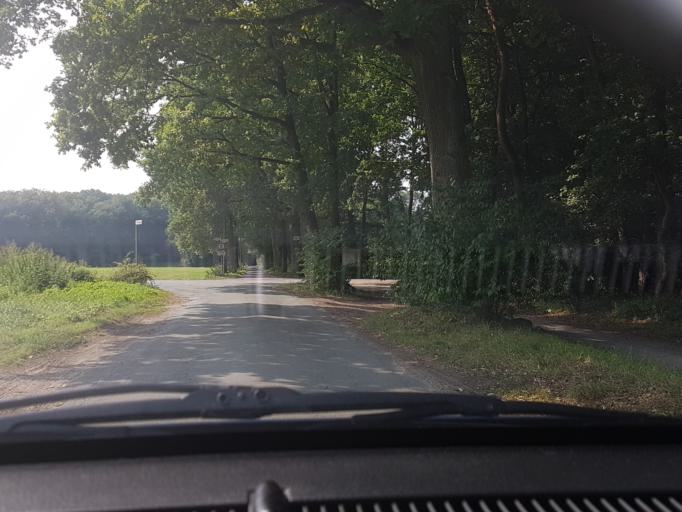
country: DE
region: North Rhine-Westphalia
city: Emsdetten
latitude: 52.1595
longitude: 7.5062
